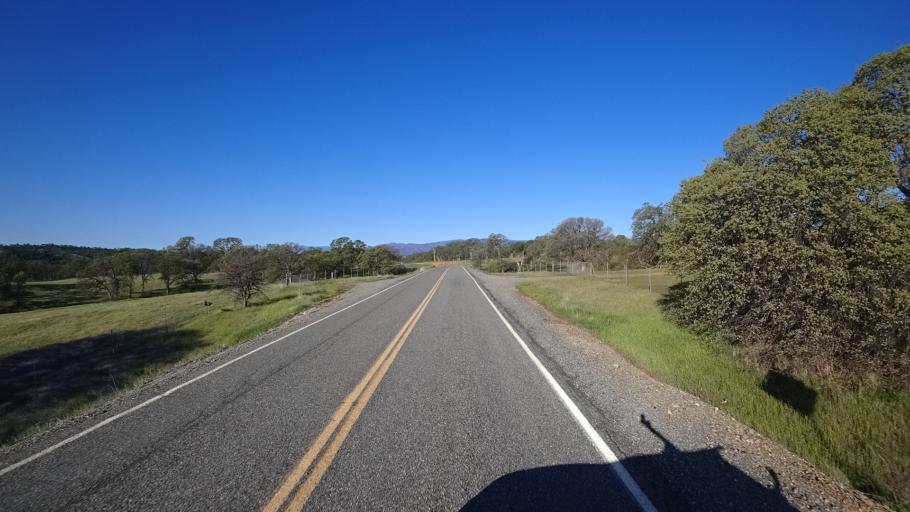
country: US
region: California
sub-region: Tehama County
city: Rancho Tehama Reserve
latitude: 39.8087
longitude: -122.4223
